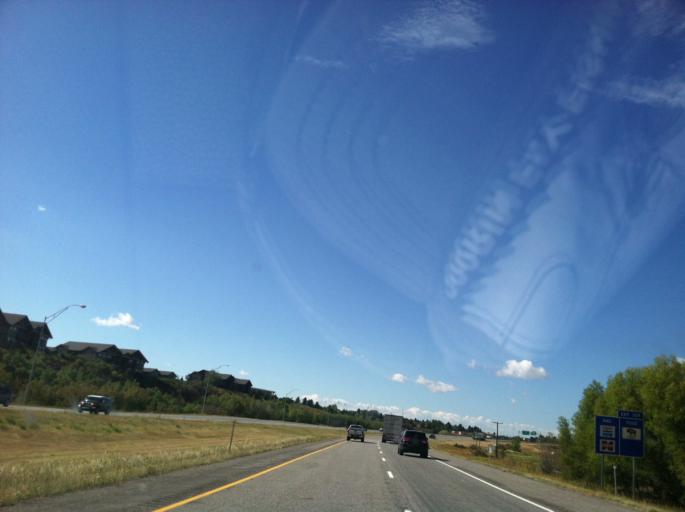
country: US
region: Montana
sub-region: Gallatin County
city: Bozeman
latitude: 45.6727
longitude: -111.0057
